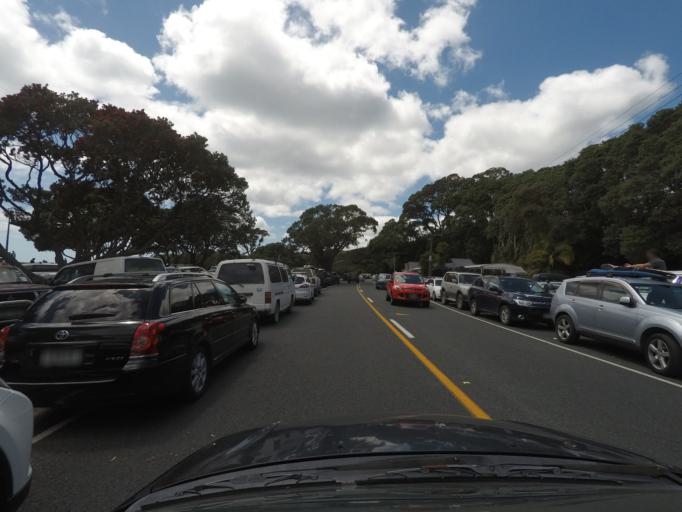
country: NZ
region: Northland
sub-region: Whangarei
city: Ruakaka
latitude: -36.0297
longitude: 174.5068
